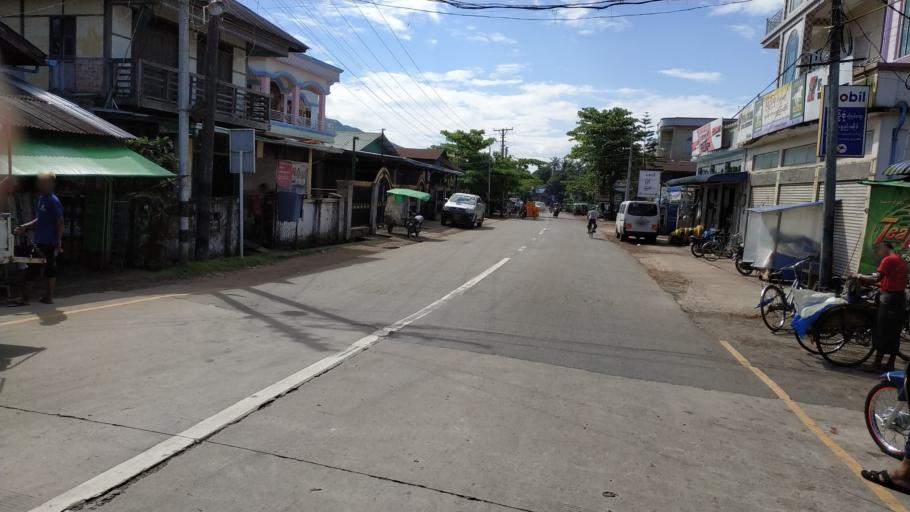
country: MM
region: Mon
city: Thaton
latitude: 16.9126
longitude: 97.3702
